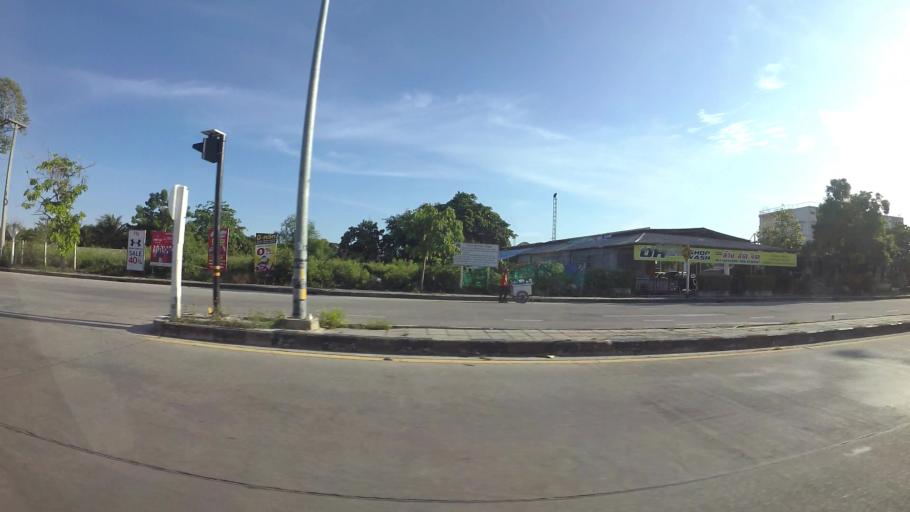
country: TH
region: Rayong
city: Rayong
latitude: 12.6844
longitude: 101.2861
